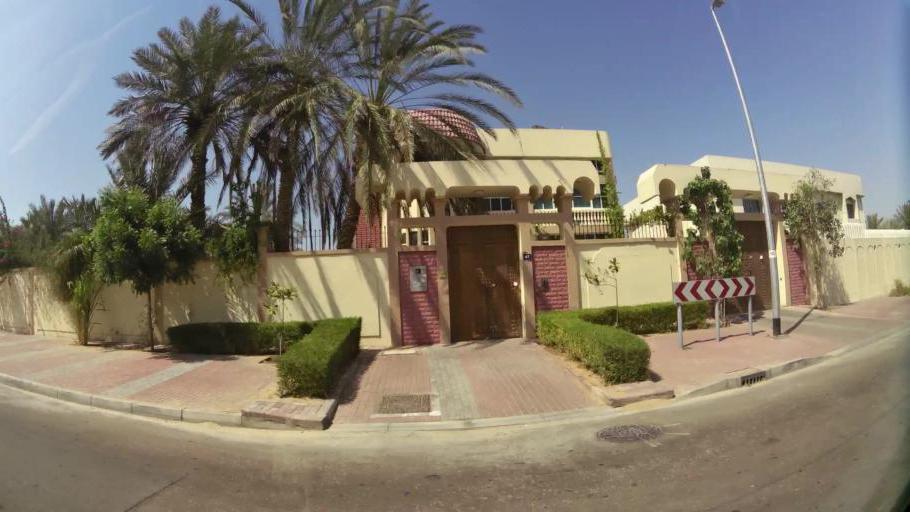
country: AE
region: Ash Shariqah
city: Sharjah
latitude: 25.2669
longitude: 55.3683
